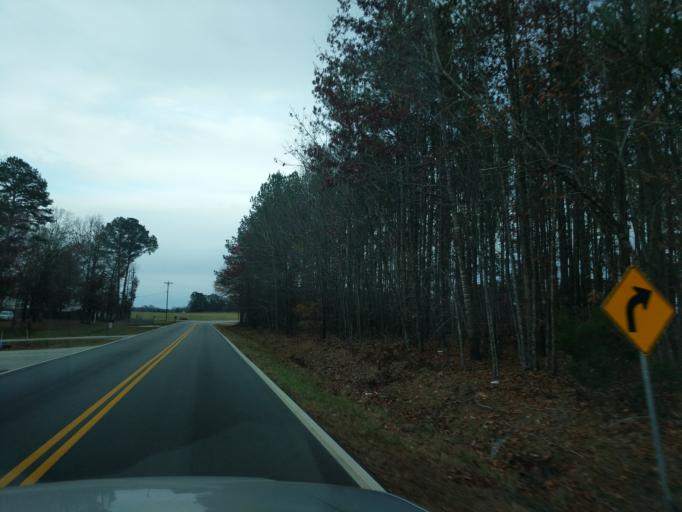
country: US
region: South Carolina
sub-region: Laurens County
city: Laurens
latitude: 34.3744
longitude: -81.9985
